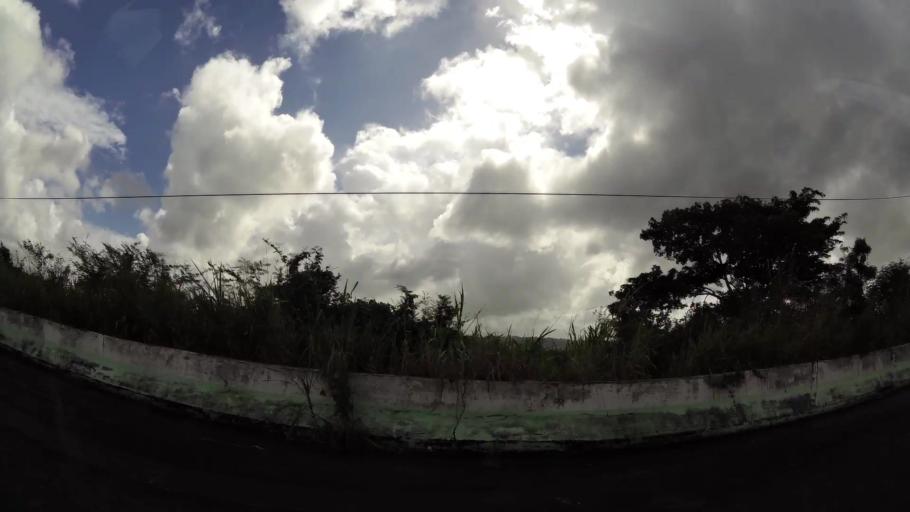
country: MQ
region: Martinique
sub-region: Martinique
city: Ducos
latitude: 14.5423
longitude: -60.9767
